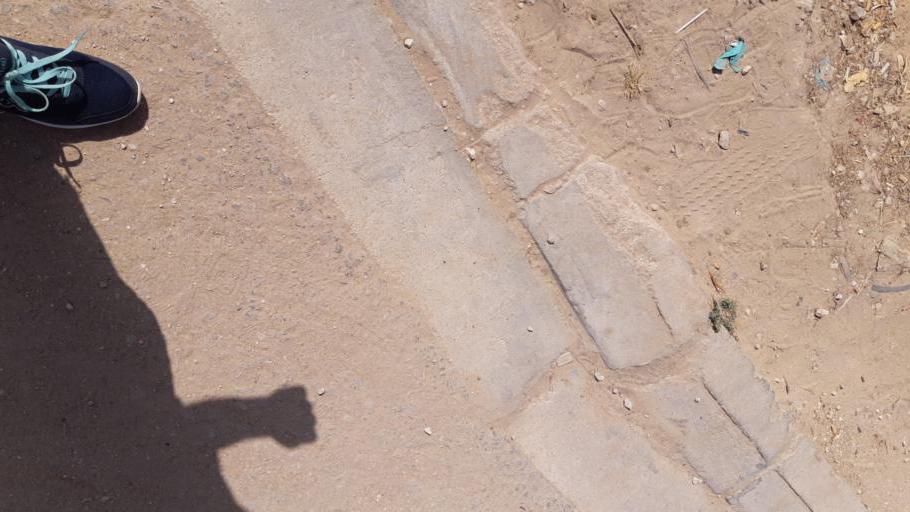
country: TN
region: Qabis
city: Gabes
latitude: 33.8676
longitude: 10.0808
